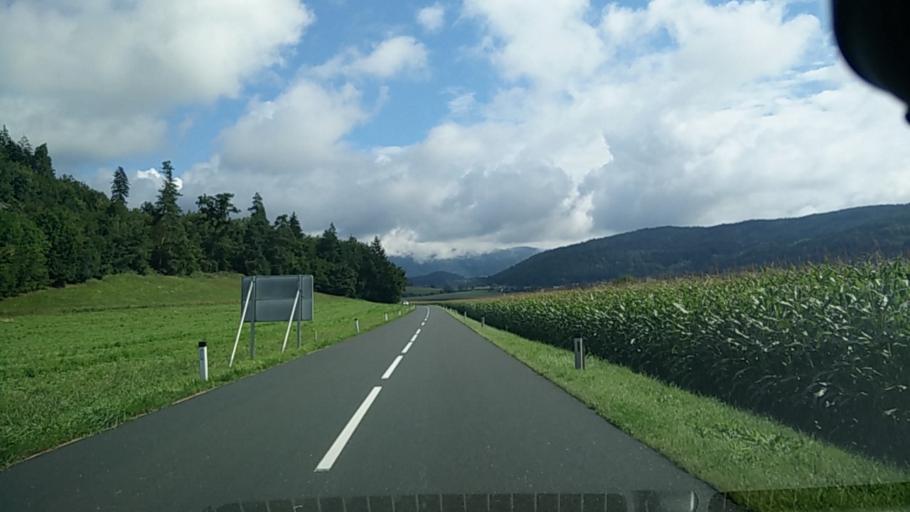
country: AT
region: Carinthia
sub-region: Politischer Bezirk Volkermarkt
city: Voelkermarkt
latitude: 46.6548
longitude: 14.5664
